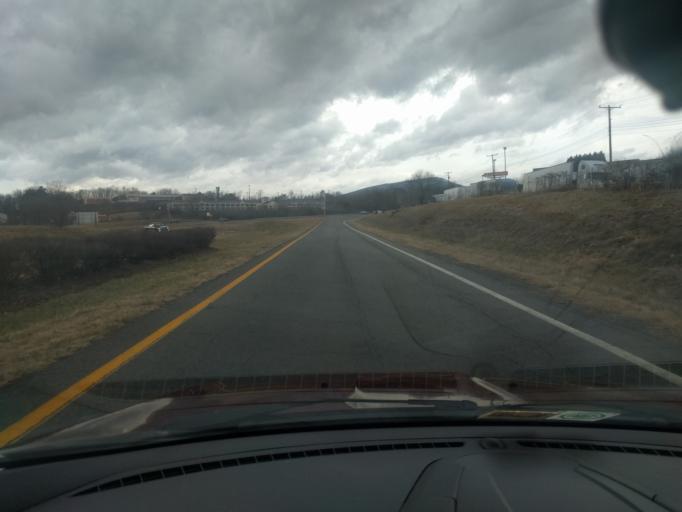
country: US
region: Virginia
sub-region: Roanoke County
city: Hollins
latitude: 37.3291
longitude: -79.9882
